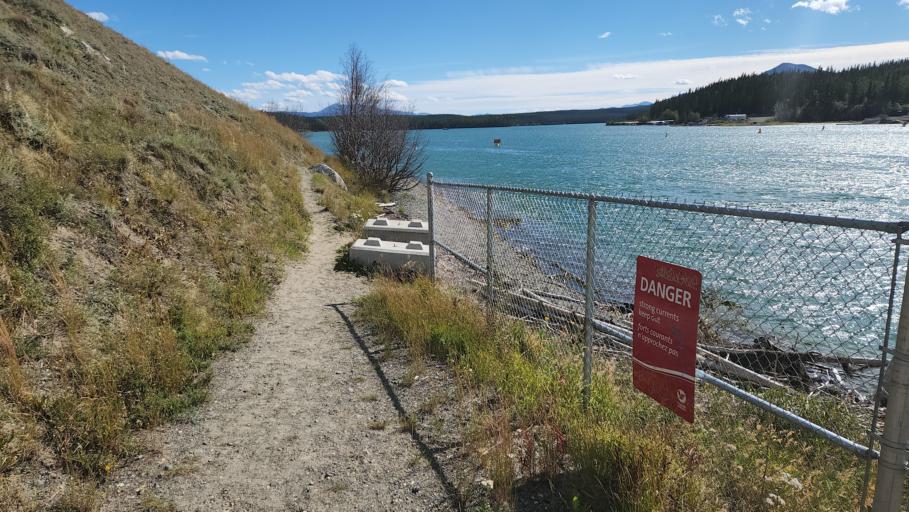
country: CA
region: Yukon
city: Whitehorse
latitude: 60.6940
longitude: -135.0380
